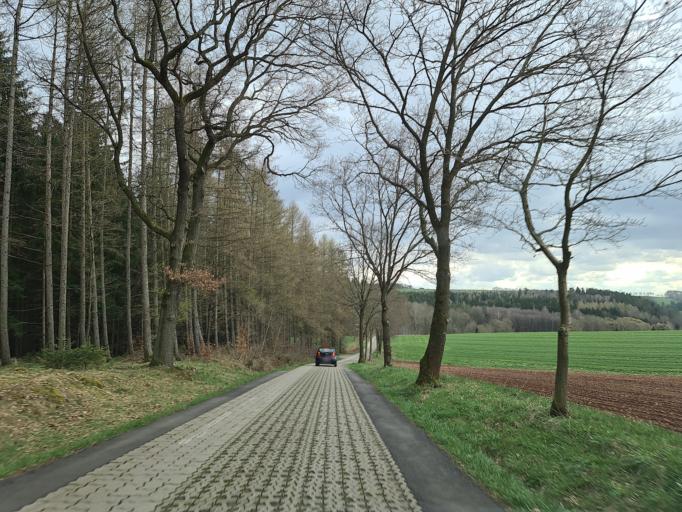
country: DE
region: Saxony
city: Lichtenstein
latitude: 50.7337
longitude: 12.6211
